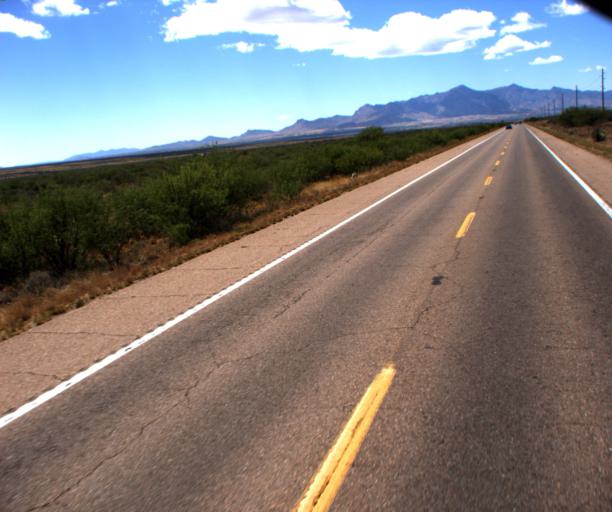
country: US
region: Arizona
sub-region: Cochise County
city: Naco
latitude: 31.3770
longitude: -110.0154
